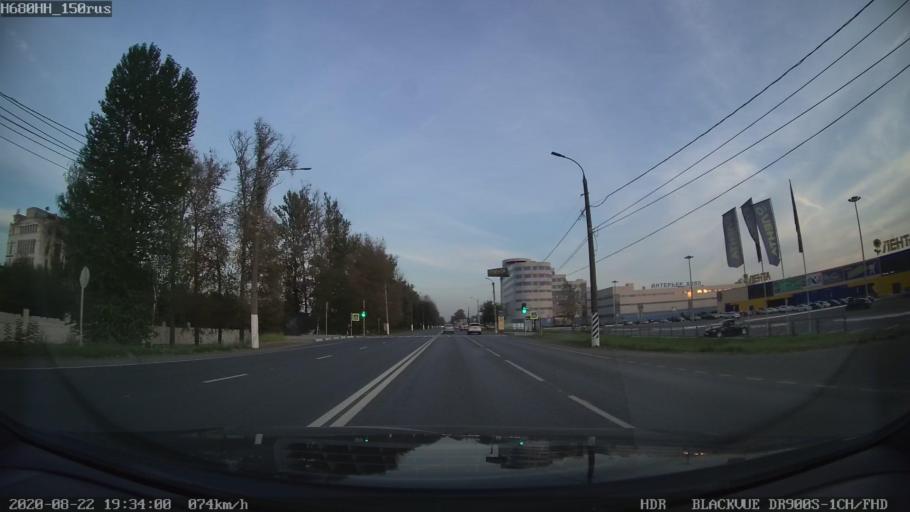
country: RU
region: Tverskaya
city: Tver
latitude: 56.8449
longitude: 35.9491
